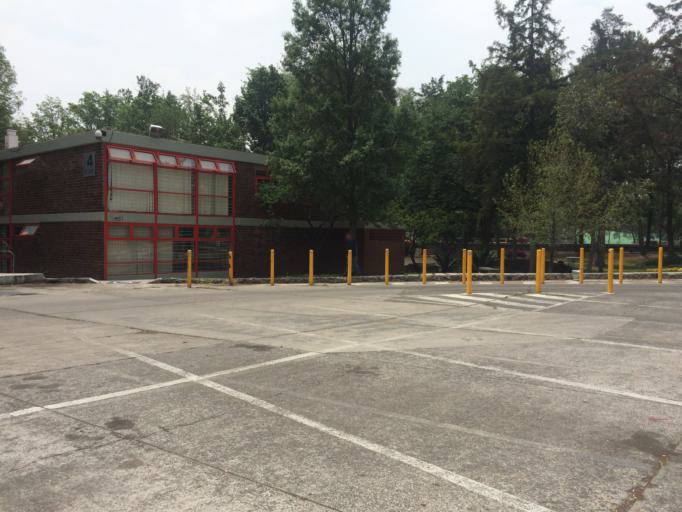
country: MX
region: Mexico City
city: Coyoacan
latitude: 19.3299
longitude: -99.1808
